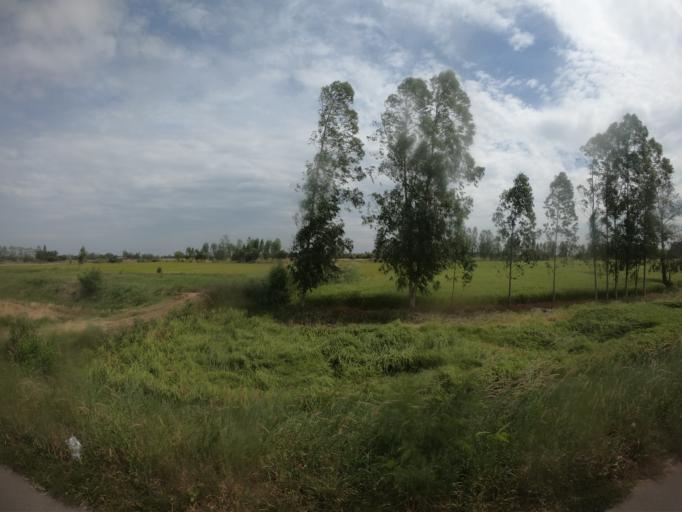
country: TH
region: Maha Sarakham
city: Chiang Yuen
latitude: 16.3794
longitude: 103.1037
